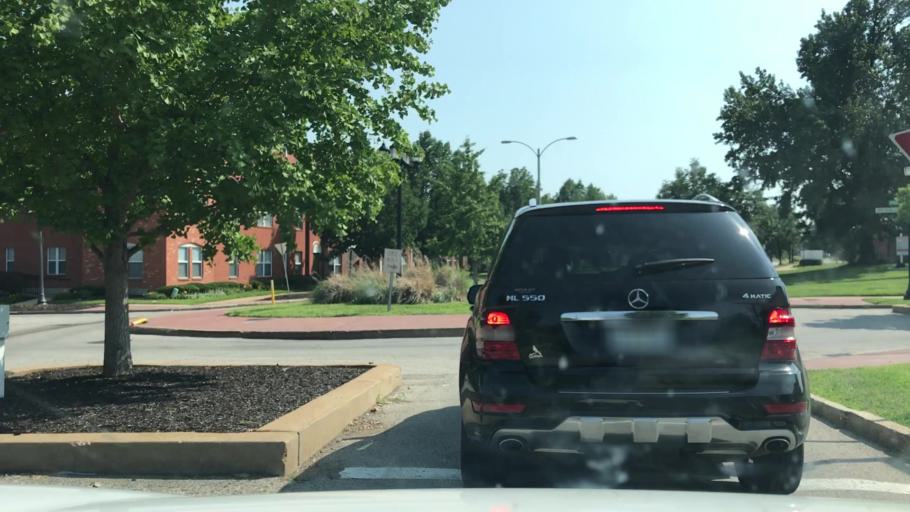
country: US
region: Missouri
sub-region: City of Saint Louis
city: St. Louis
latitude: 38.6155
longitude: -90.2059
